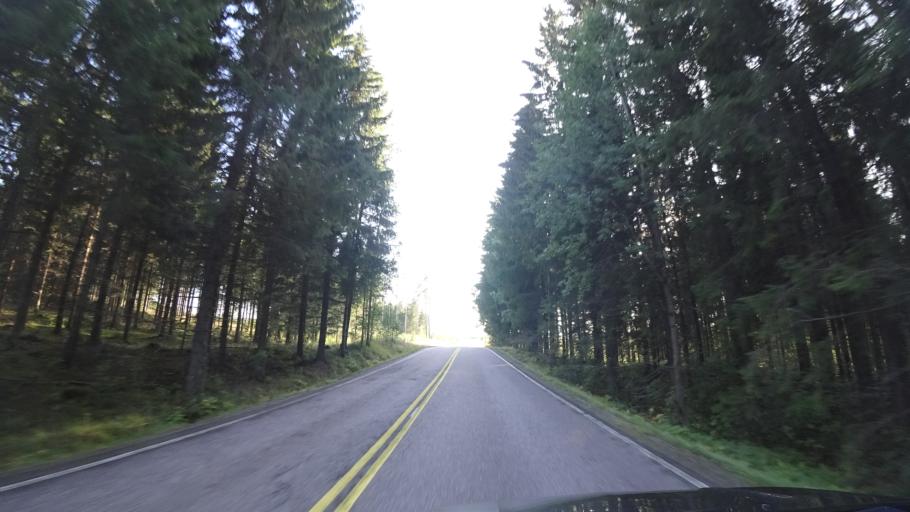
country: FI
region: Paijanne Tavastia
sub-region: Lahti
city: Hollola
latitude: 61.1677
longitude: 25.3663
